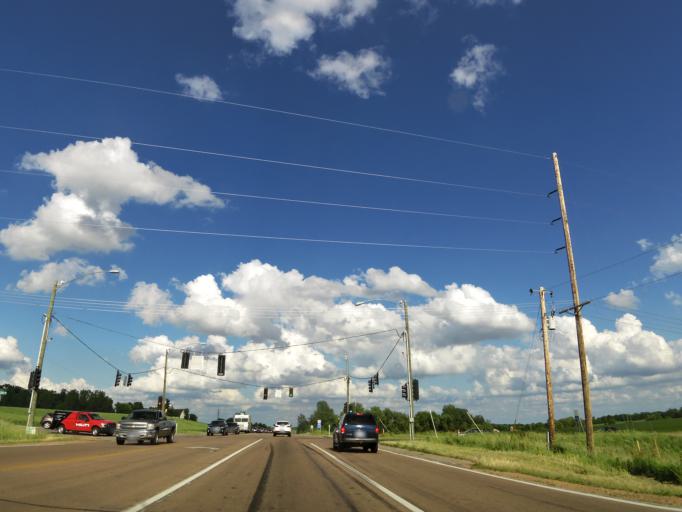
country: US
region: Minnesota
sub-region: Carver County
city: Victoria
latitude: 44.8078
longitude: -93.6532
